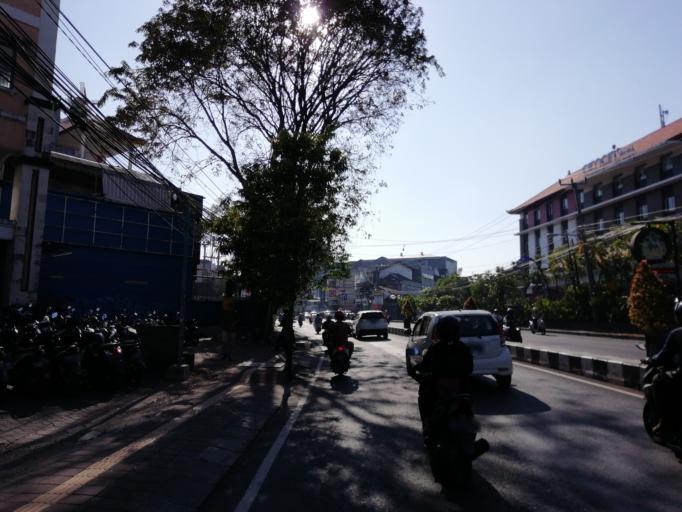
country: ID
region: Bali
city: Karyadharma
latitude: -8.6808
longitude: 115.2025
